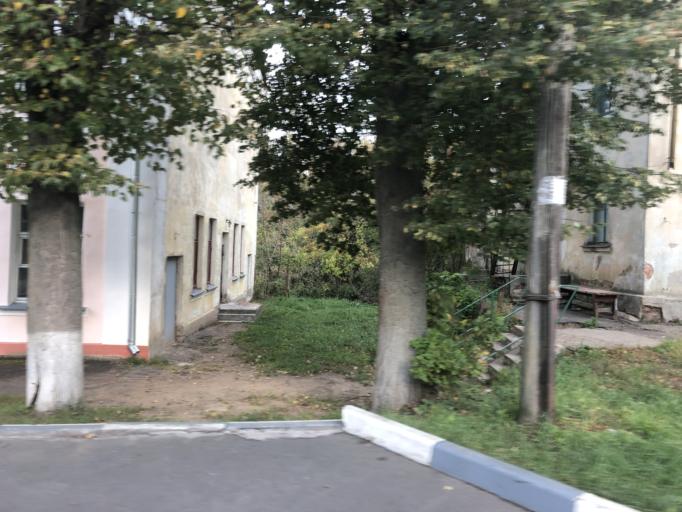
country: RU
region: Tverskaya
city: Rzhev
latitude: 56.2553
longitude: 34.2930
